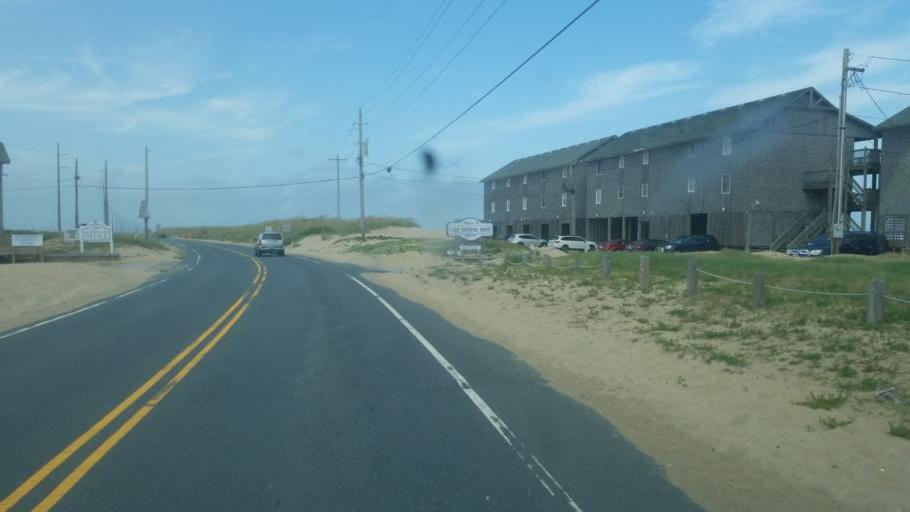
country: US
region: North Carolina
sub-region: Dare County
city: Buxton
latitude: 35.2670
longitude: -75.5192
